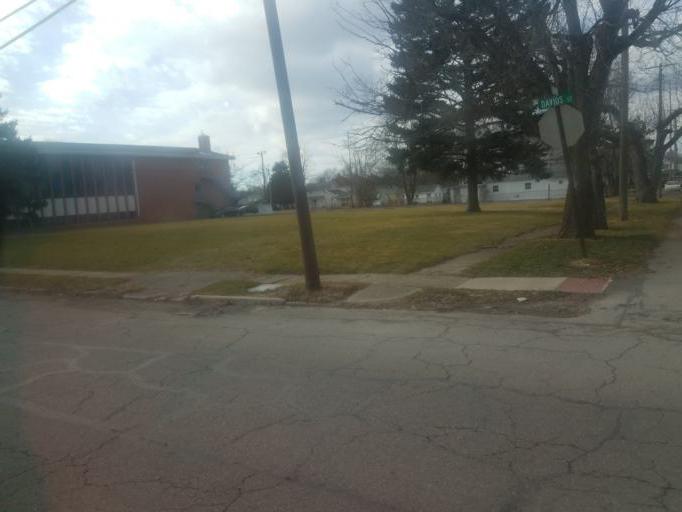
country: US
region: Ohio
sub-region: Marion County
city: Marion
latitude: 40.5813
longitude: -83.1433
